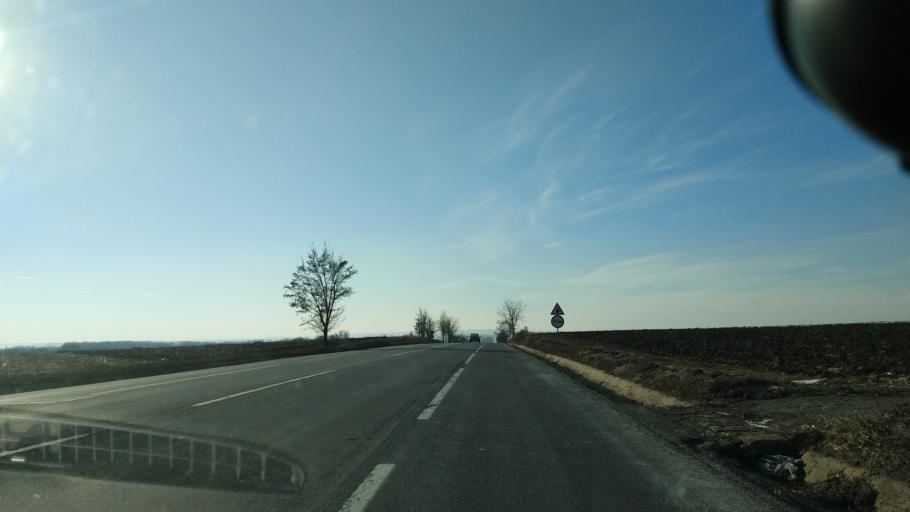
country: RO
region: Iasi
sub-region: Comuna Butea
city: Butea
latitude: 47.0895
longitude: 26.9139
